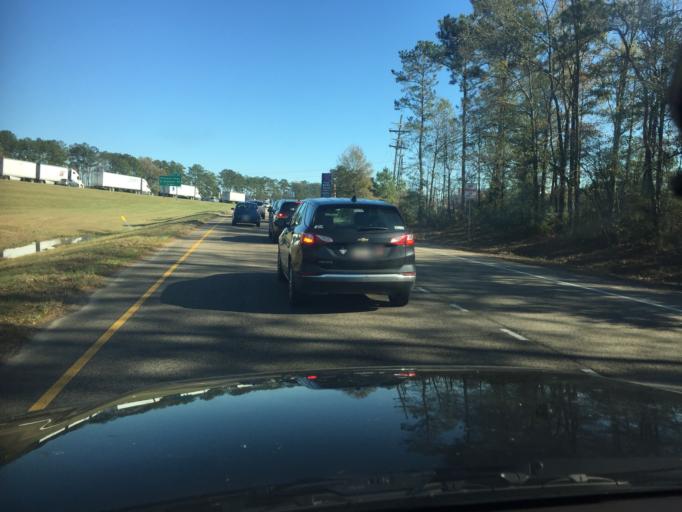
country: US
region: Louisiana
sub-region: Saint Tammany Parish
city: Covington
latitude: 30.4457
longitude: -90.1395
